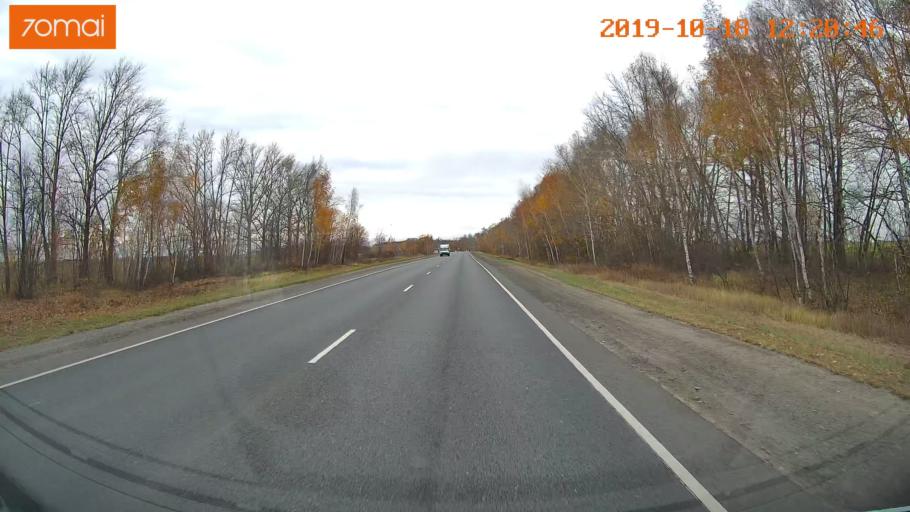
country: RU
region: Rjazan
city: Bagramovo
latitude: 54.5027
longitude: 39.4842
